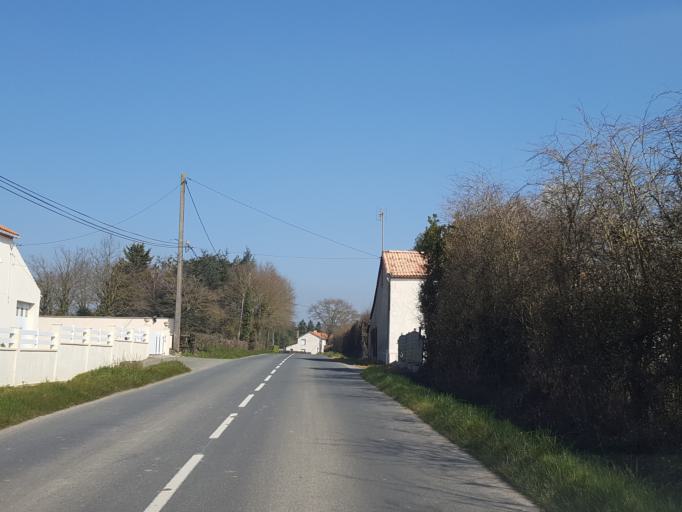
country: FR
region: Pays de la Loire
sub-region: Departement de la Vendee
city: La Chaize-le-Vicomte
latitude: 46.6588
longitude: -1.2988
